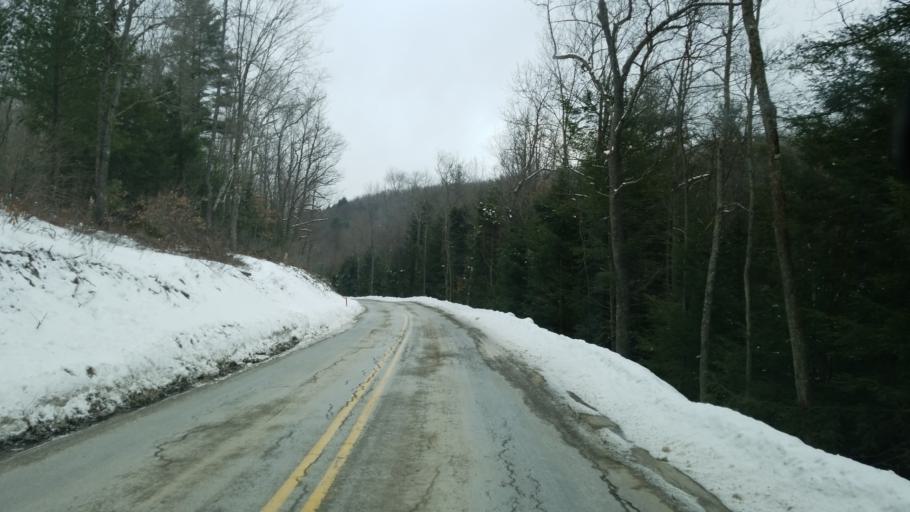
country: US
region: Pennsylvania
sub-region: Clearfield County
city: Shiloh
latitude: 41.2396
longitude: -78.1757
